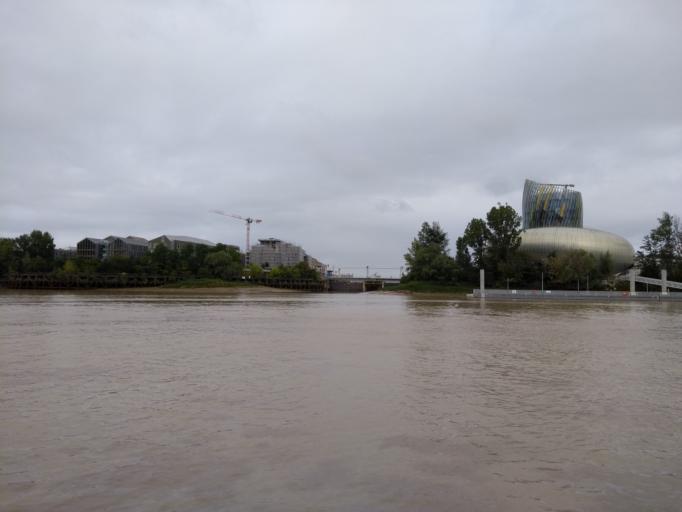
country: FR
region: Aquitaine
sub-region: Departement de la Gironde
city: Cenon
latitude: 44.8602
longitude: -0.5482
